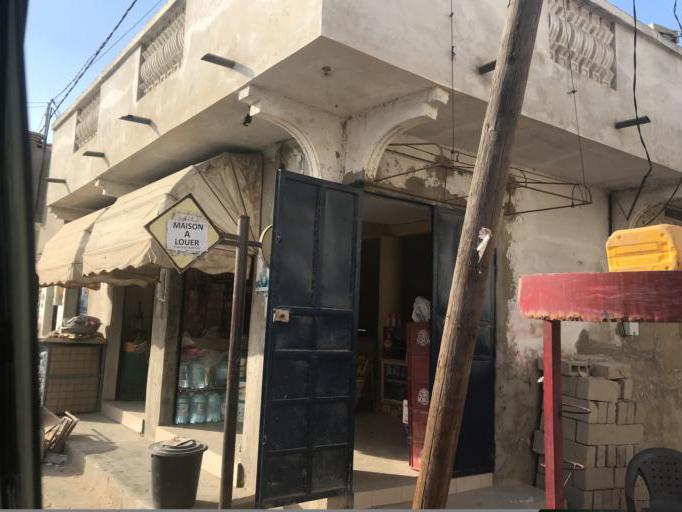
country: SN
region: Saint-Louis
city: Saint-Louis
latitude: 15.9990
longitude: -16.4956
